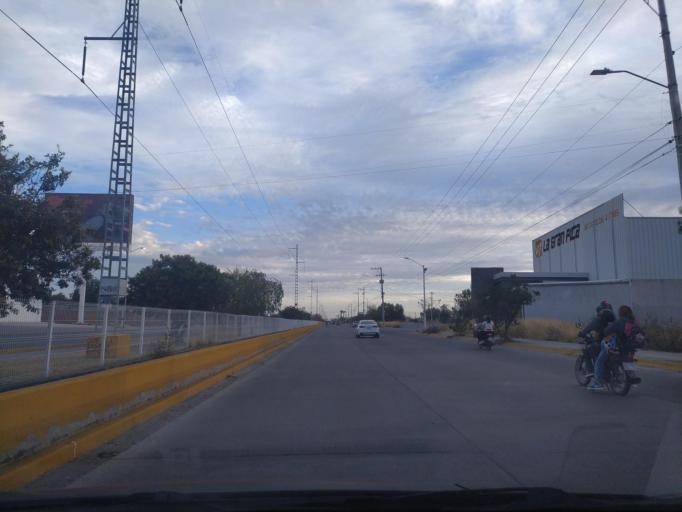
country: LA
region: Oudomxai
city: Muang La
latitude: 21.0223
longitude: 101.8696
